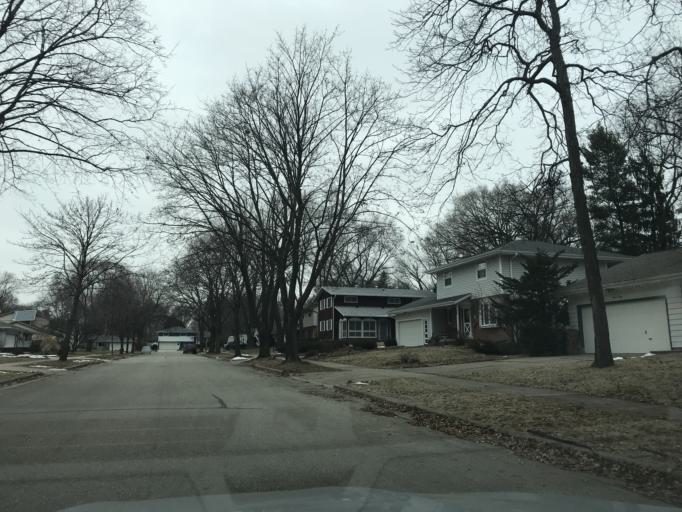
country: US
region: Wisconsin
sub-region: Dane County
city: Monona
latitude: 43.0905
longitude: -89.2998
